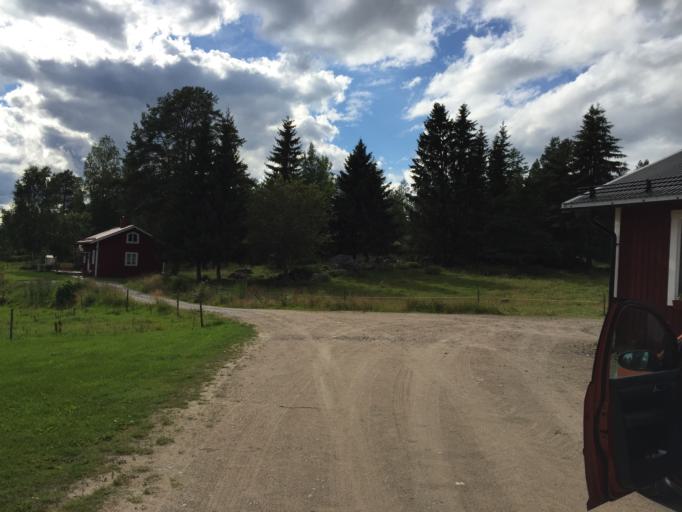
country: SE
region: Gaevleborg
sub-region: Ljusdals Kommun
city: Jaervsoe
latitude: 61.7752
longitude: 16.2034
